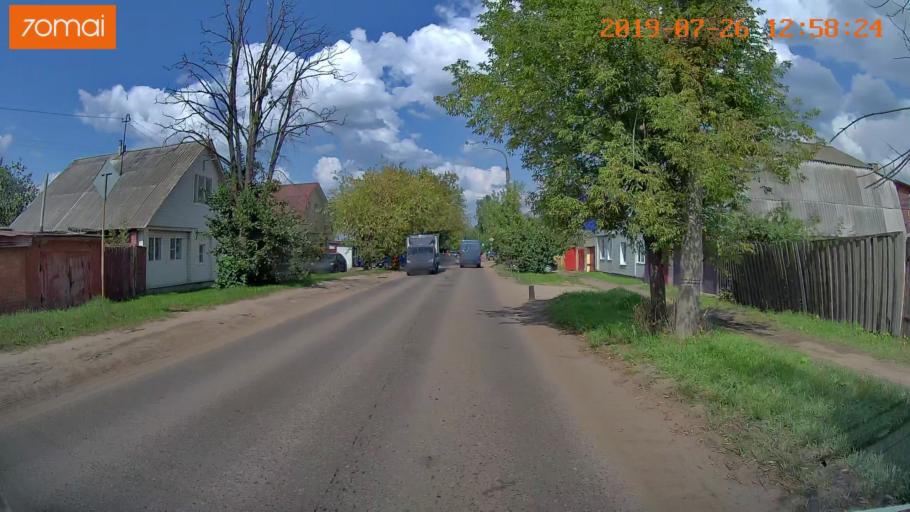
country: RU
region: Ivanovo
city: Bogorodskoye
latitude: 57.0239
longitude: 41.0208
